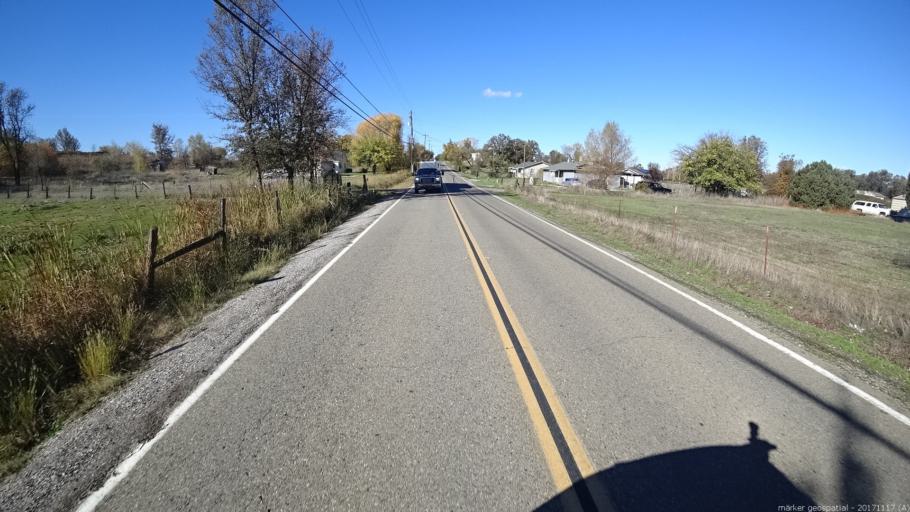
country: US
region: California
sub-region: Shasta County
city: Cottonwood
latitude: 40.4219
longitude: -122.2191
